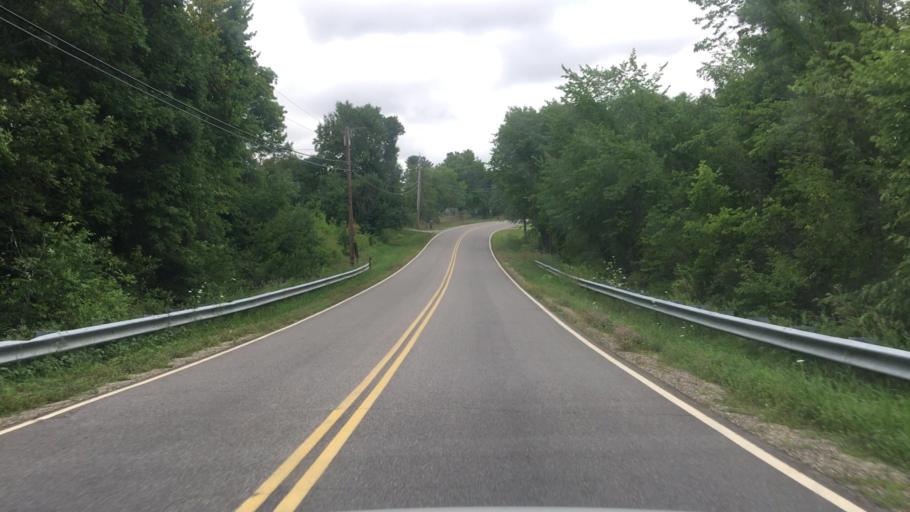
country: US
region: Maine
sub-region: York County
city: Dayton
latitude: 43.5219
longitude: -70.5201
